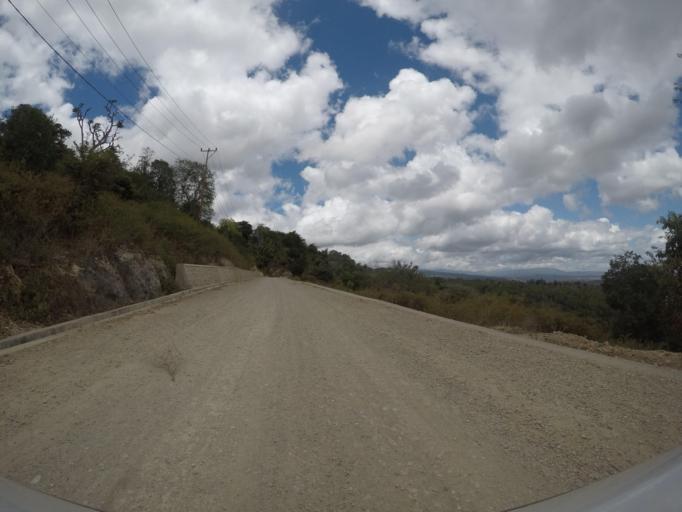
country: TL
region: Lautem
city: Lospalos
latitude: -8.3750
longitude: 126.9259
